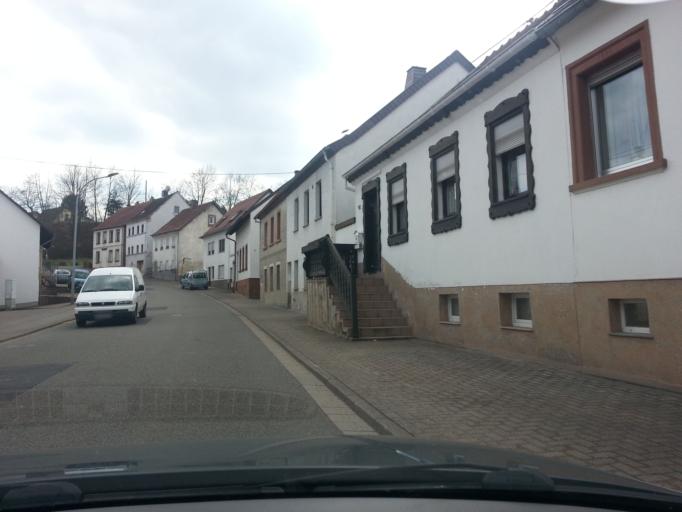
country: DE
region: Saarland
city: Bexbach
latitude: 49.3445
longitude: 7.2208
